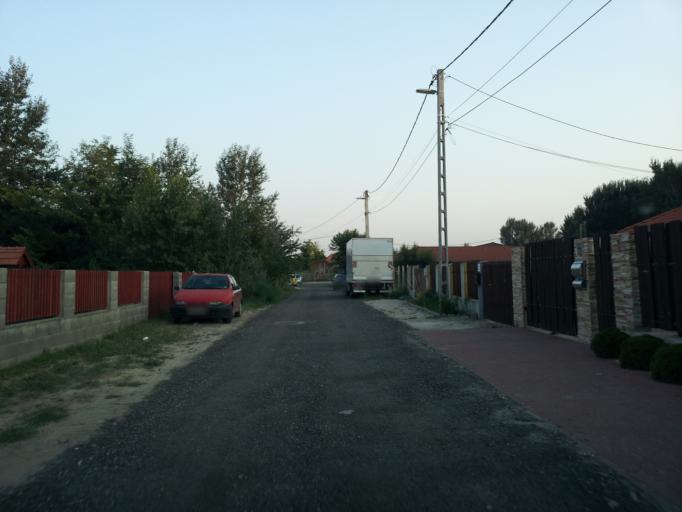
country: HU
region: Pest
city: Szigetszentmiklos
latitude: 47.3316
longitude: 19.0287
